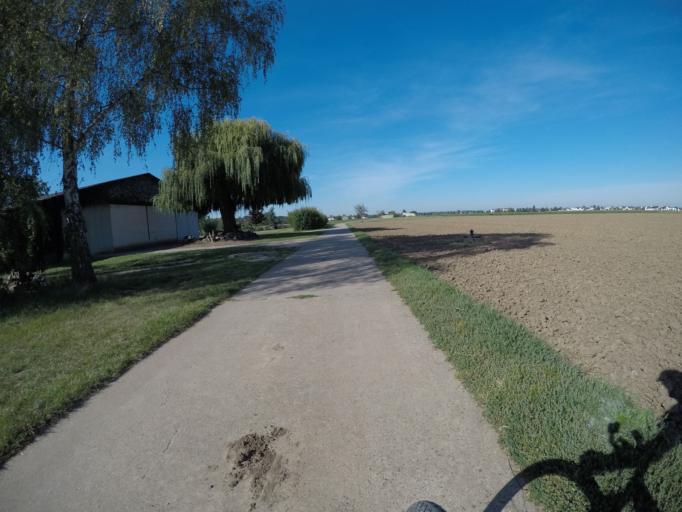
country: DE
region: Hesse
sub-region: Regierungsbezirk Darmstadt
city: Riedstadt
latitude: 49.8247
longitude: 8.5136
